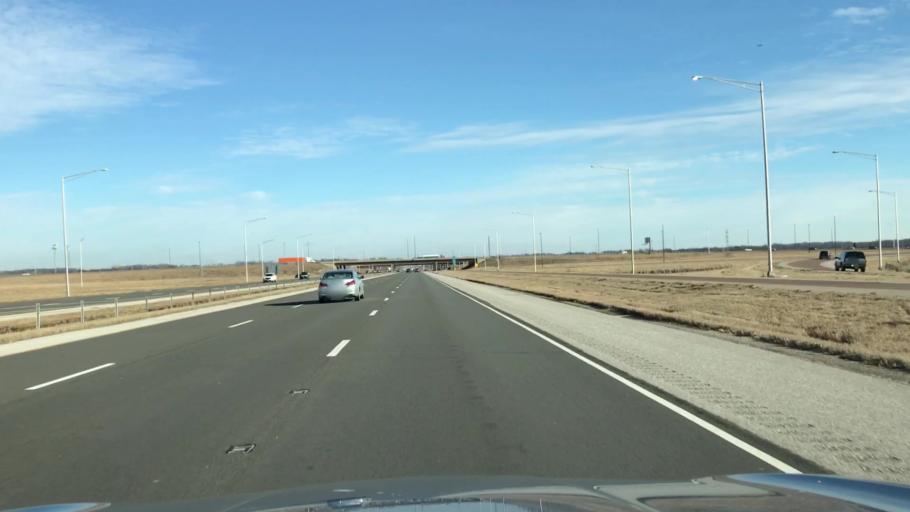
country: US
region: Illinois
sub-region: Madison County
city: Mitchell
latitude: 38.7572
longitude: -90.0498
